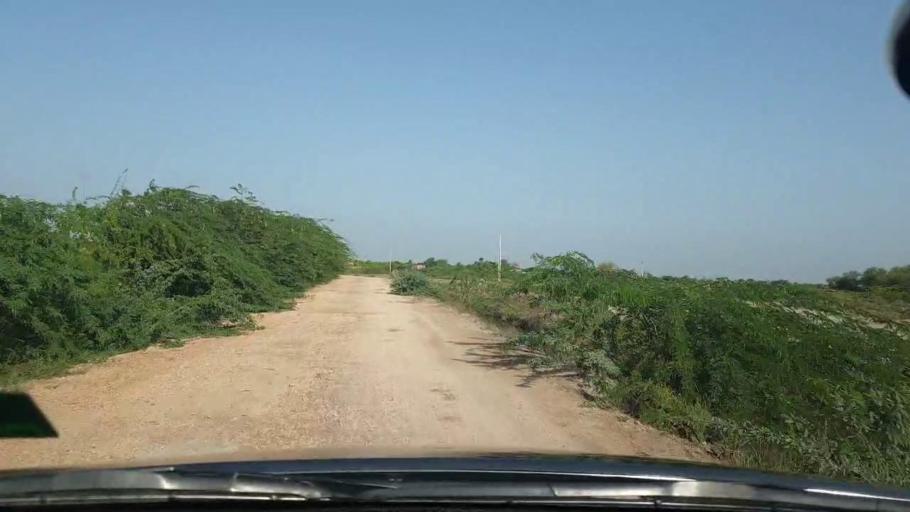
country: PK
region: Sindh
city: Tando Bago
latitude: 24.6853
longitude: 69.0109
